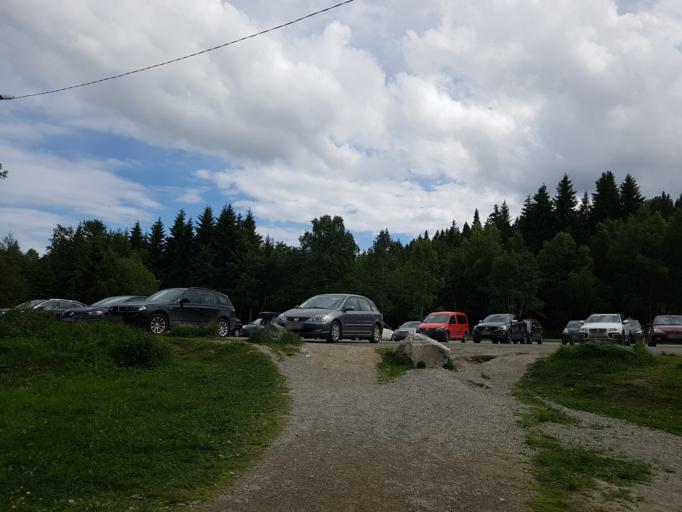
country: NO
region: Sor-Trondelag
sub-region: Trondheim
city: Trondheim
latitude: 63.4167
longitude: 10.3236
